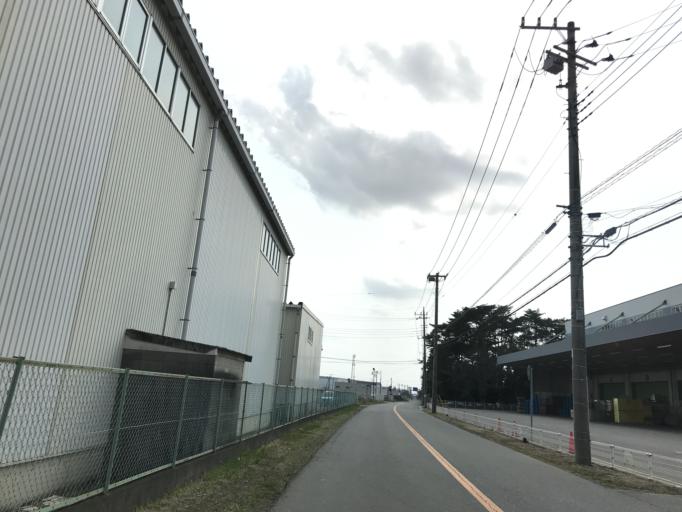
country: JP
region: Ibaraki
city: Ushiku
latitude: 35.9985
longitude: 140.0689
